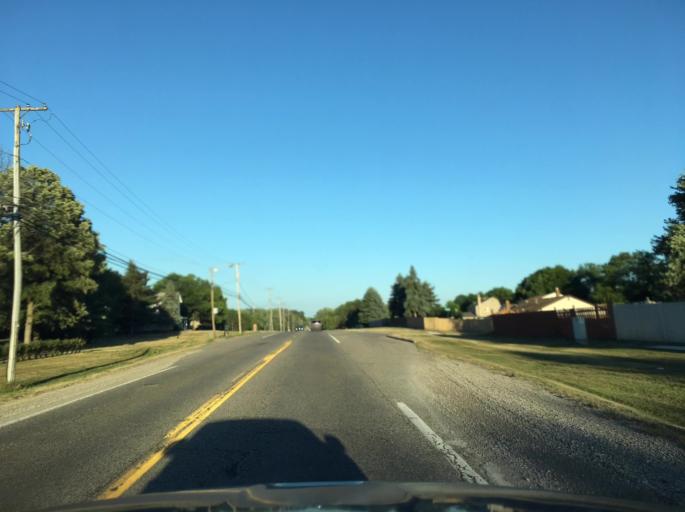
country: US
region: Michigan
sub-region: Macomb County
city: Fraser
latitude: 42.5741
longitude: -82.9821
